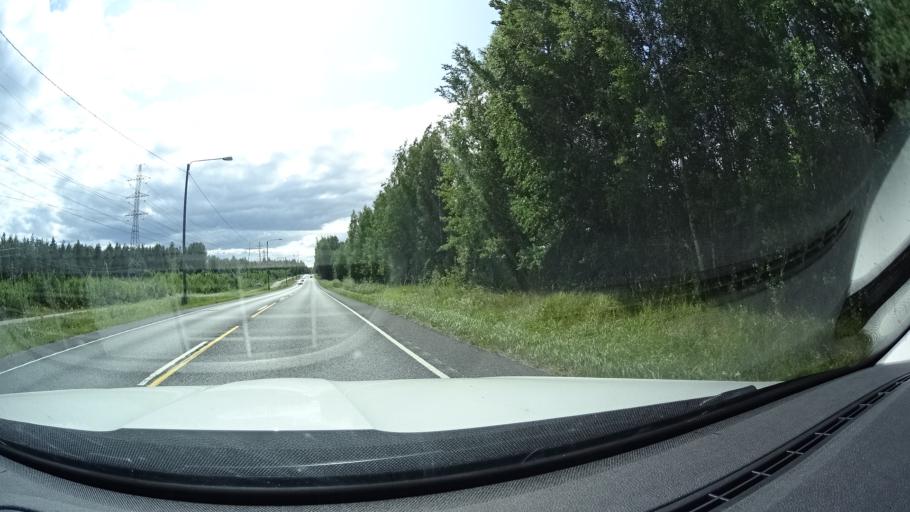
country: FI
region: Uusimaa
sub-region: Helsinki
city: Kerava
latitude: 60.3236
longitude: 25.1184
